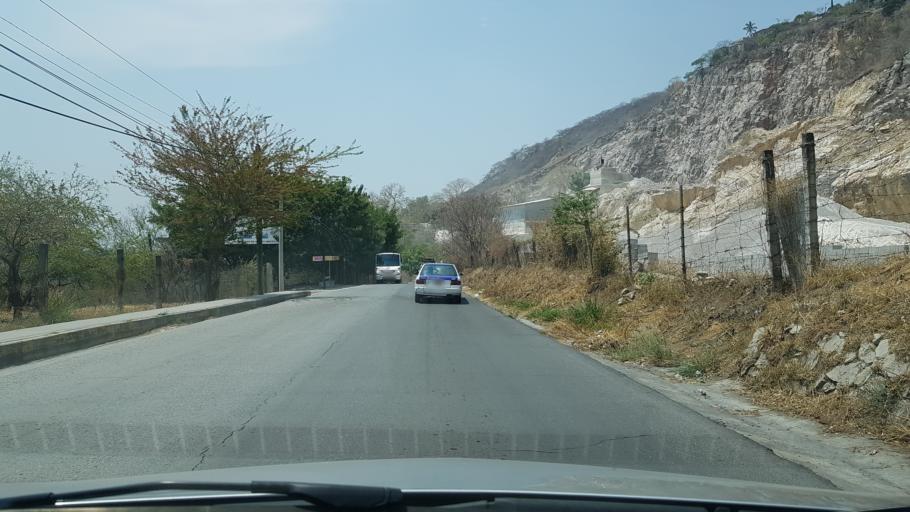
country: MX
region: Morelos
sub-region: Jiutepec
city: Jiutepec
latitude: 18.8715
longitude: -99.1731
